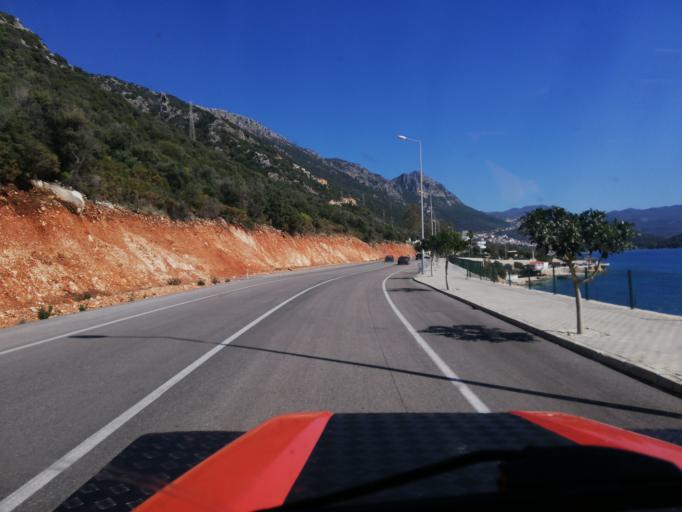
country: TR
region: Antalya
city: Kas
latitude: 36.2087
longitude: 29.6115
